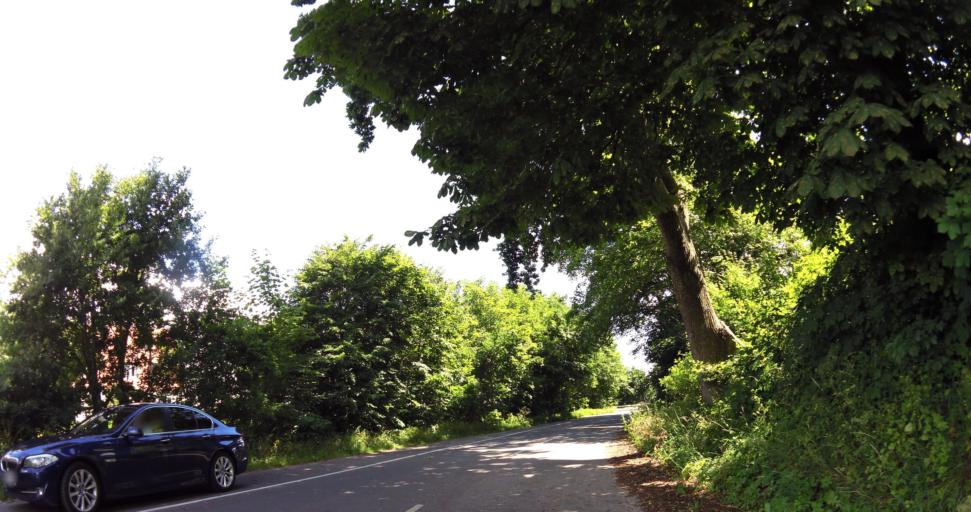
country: DE
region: Schleswig-Holstein
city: Brodersby
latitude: 54.5225
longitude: 9.7166
